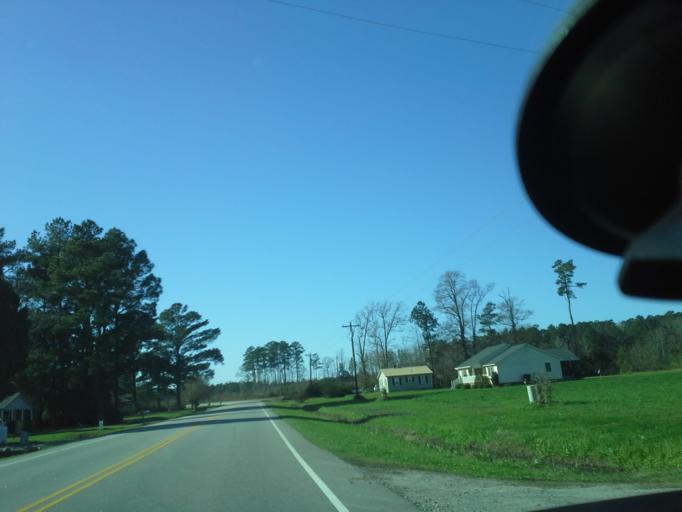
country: US
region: North Carolina
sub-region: Beaufort County
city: Belhaven
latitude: 35.5789
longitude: -76.6792
